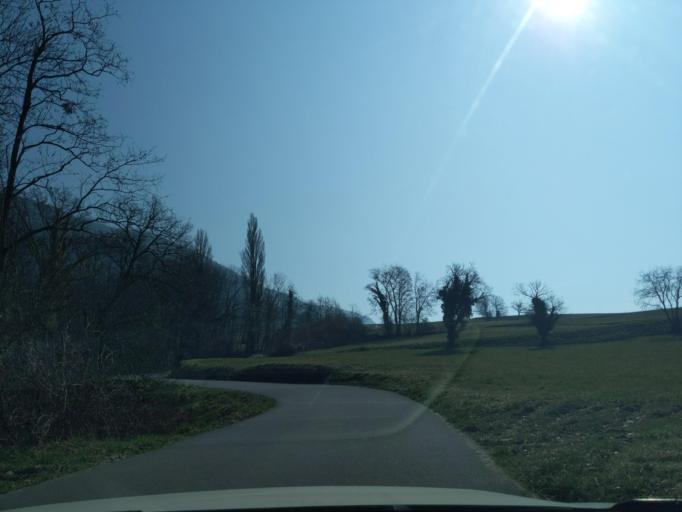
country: FR
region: Rhone-Alpes
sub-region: Departement de la Haute-Savoie
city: Versonnex
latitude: 45.9304
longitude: 5.8401
